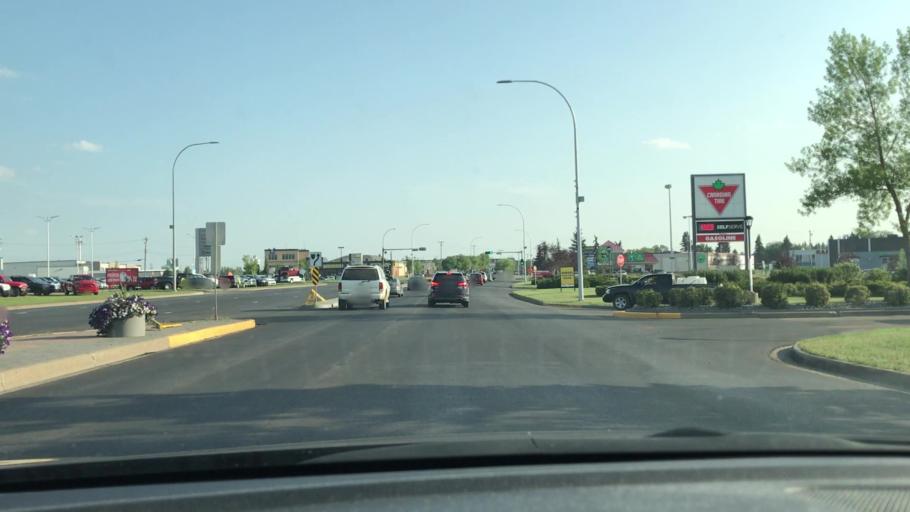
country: CA
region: Alberta
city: Leduc
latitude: 53.2762
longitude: -113.5488
